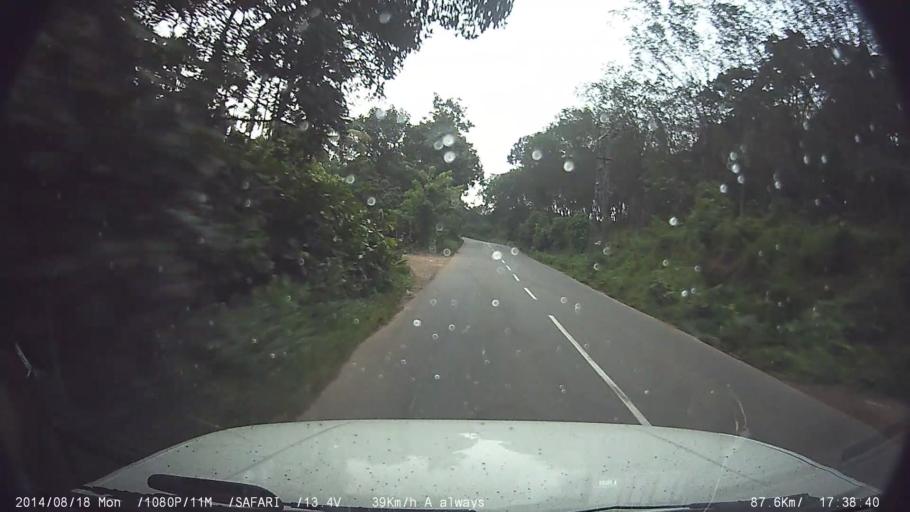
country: IN
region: Kerala
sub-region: Ernakulam
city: Muvattupuzha
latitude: 9.9178
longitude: 76.5827
